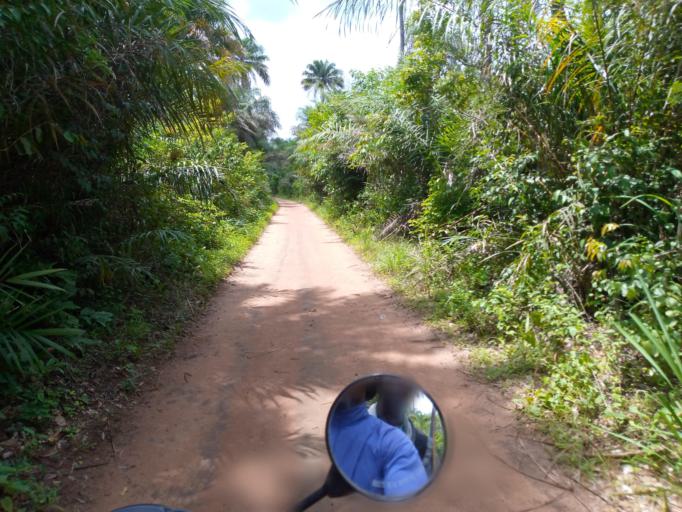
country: SL
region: Northern Province
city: Mange
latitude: 8.9739
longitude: -12.8245
